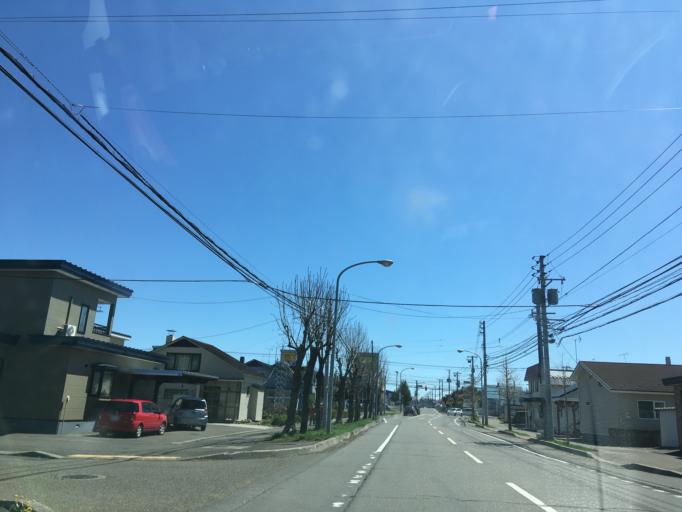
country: JP
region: Hokkaido
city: Obihiro
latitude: 42.9209
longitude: 143.1714
